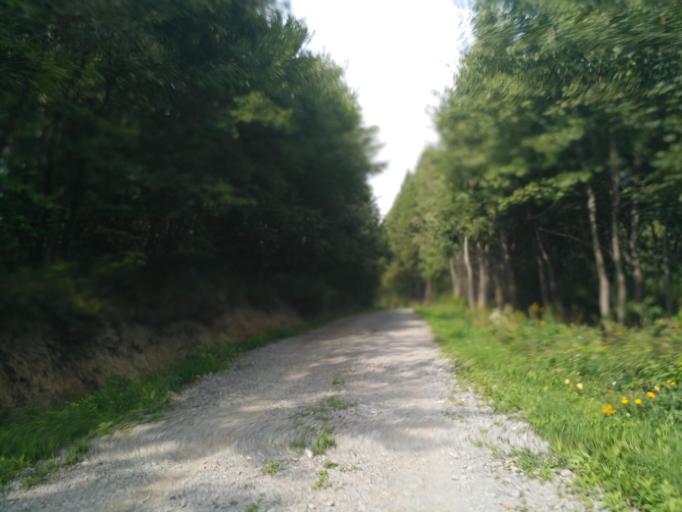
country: PL
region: Subcarpathian Voivodeship
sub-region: Powiat ropczycko-sedziszowski
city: Wielopole Skrzynskie
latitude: 49.9036
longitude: 21.6115
